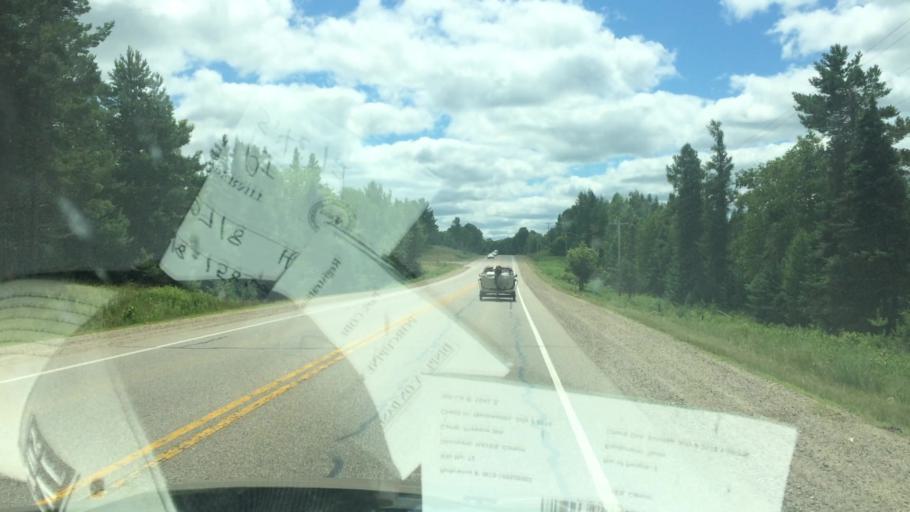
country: US
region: Wisconsin
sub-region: Vilas County
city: Eagle River
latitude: 45.7979
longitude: -89.3202
